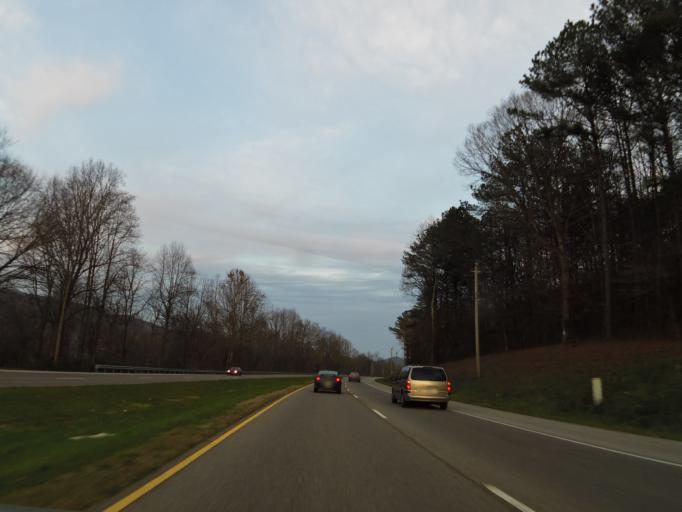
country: US
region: Tennessee
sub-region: Roane County
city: Rockwood
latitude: 35.8865
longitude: -84.6510
